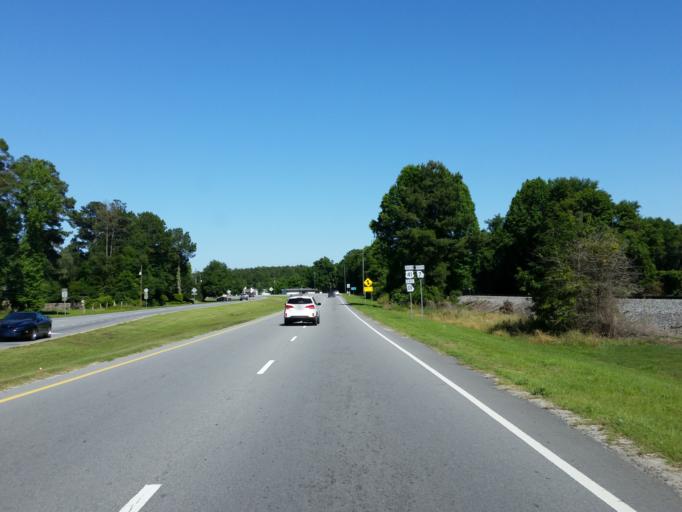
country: US
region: Georgia
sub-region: Lowndes County
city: Valdosta
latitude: 30.6870
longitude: -83.1991
